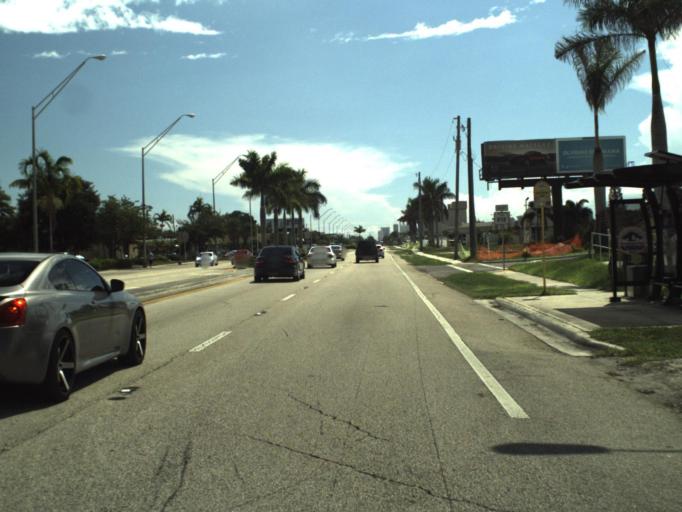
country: US
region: Florida
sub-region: Broward County
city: Carver Ranches
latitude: 25.9842
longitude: -80.1911
